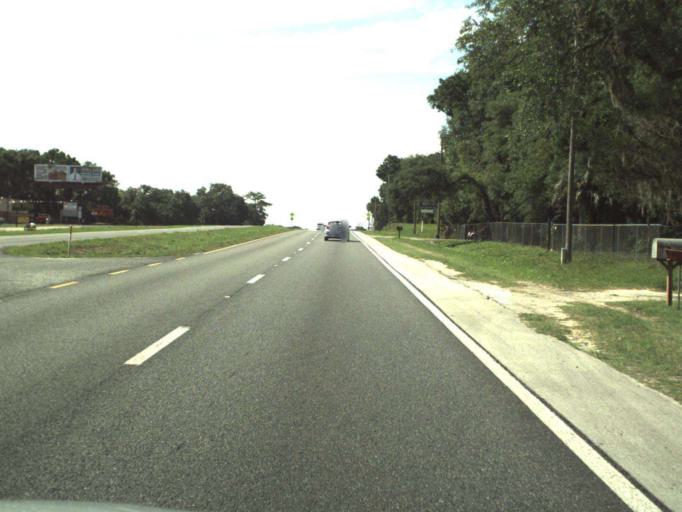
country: US
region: Florida
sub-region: Marion County
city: Belleview
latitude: 29.0801
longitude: -82.0764
